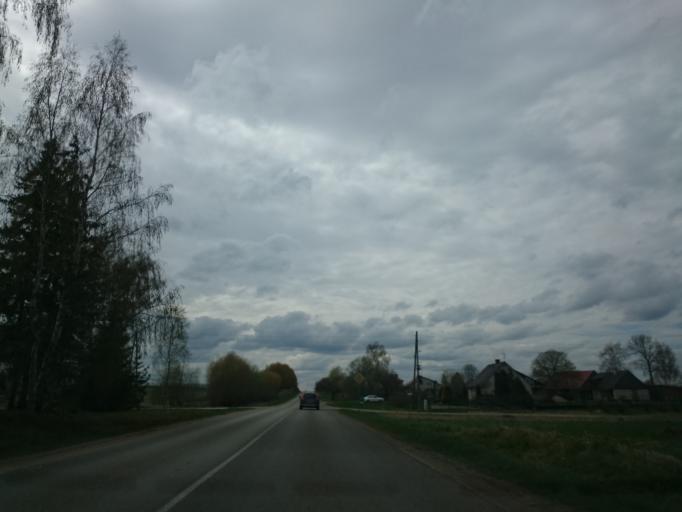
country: LV
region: Tukuma Rajons
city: Tukums
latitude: 56.9323
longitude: 23.0872
